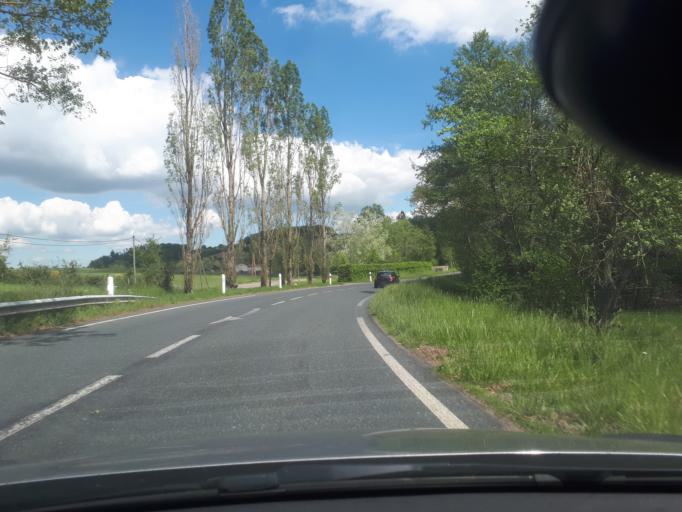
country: FR
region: Rhone-Alpes
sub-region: Departement du Rhone
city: Haute-Rivoire
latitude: 45.7252
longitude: 4.4087
